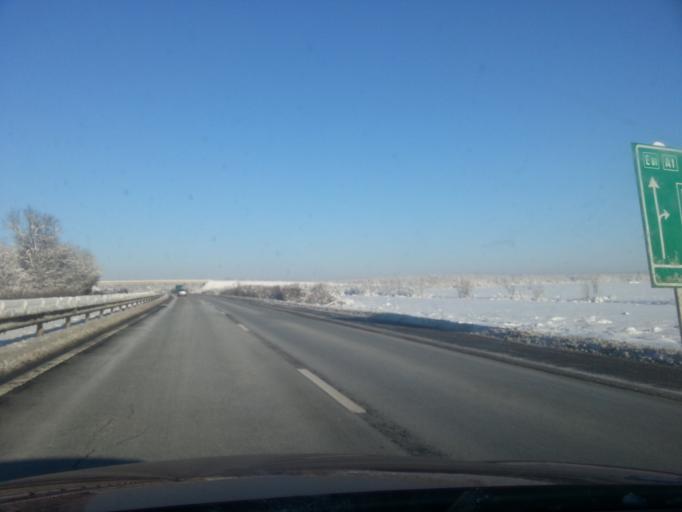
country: RO
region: Dambovita
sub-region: Comuna Corbii Mari
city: Grozavesti
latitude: 44.6001
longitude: 25.4587
